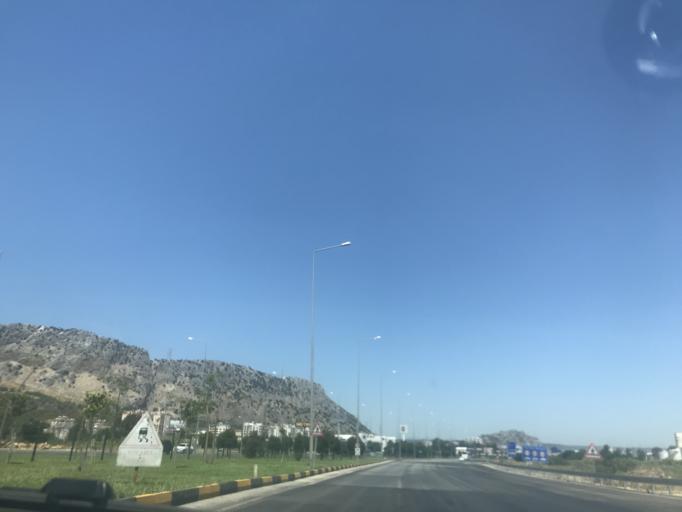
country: TR
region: Antalya
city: Cakirlar
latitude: 36.8365
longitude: 30.5958
